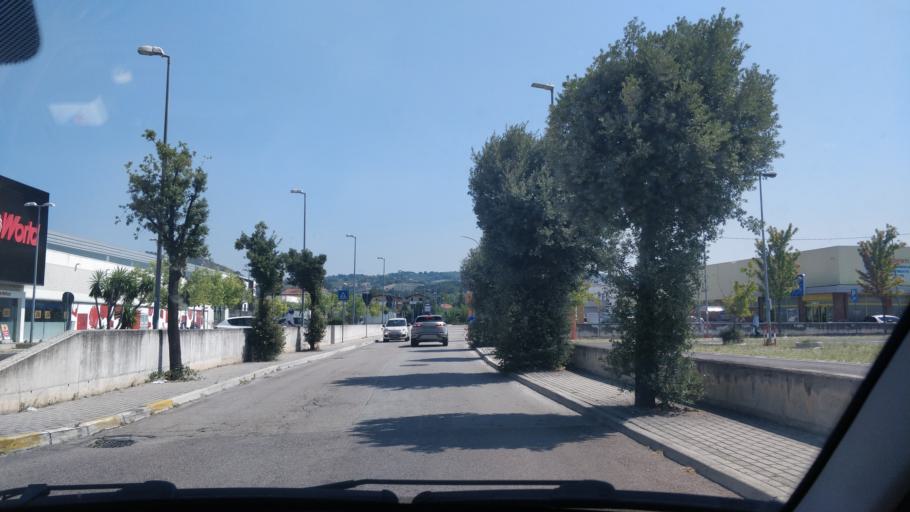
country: IT
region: Abruzzo
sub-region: Provincia di Chieti
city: Sambuceto
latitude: 42.4160
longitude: 14.1716
